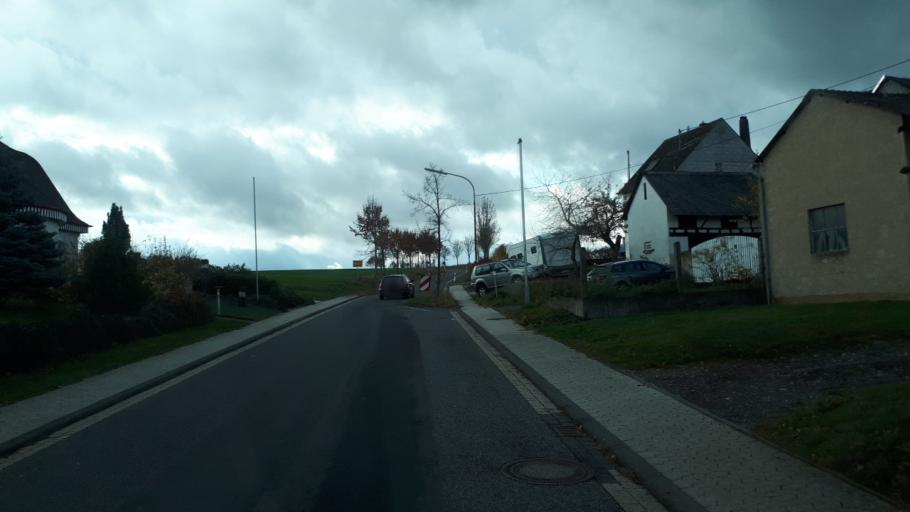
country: DE
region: Rheinland-Pfalz
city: Dunfus
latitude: 50.2191
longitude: 7.2321
